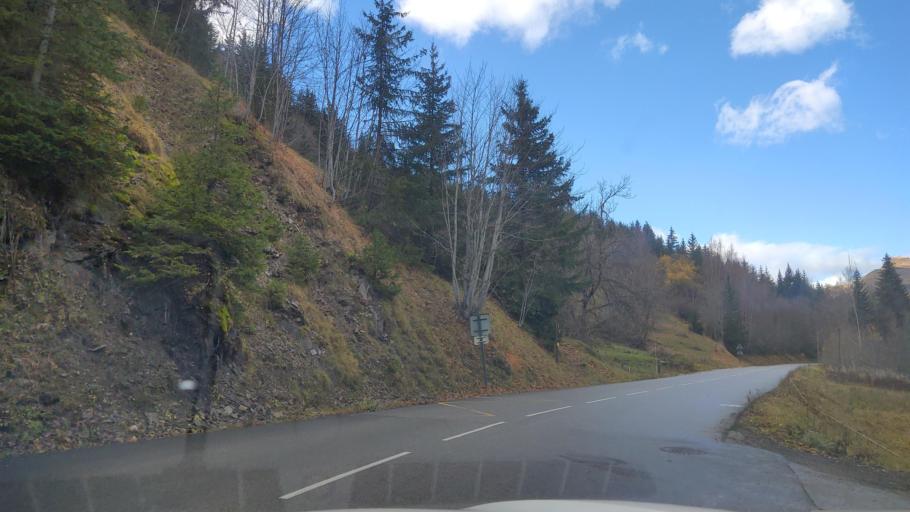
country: FR
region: Rhone-Alpes
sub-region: Departement de la Savoie
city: Saint-Jean-de-Maurienne
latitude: 45.1925
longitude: 6.2860
